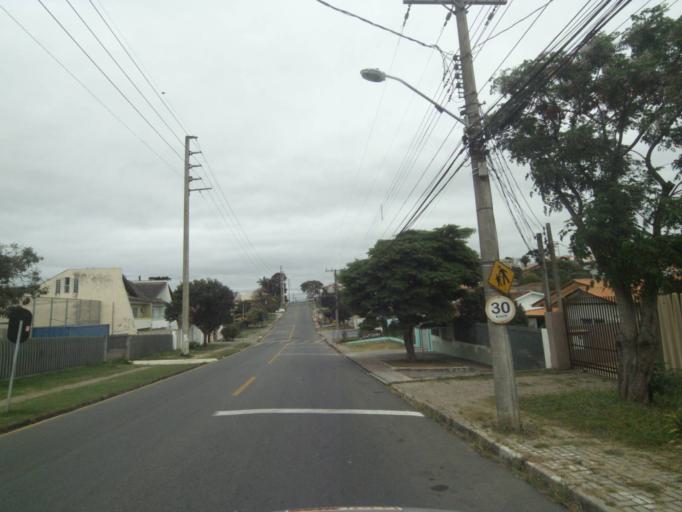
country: BR
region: Parana
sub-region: Pinhais
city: Pinhais
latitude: -25.4824
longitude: -49.2270
